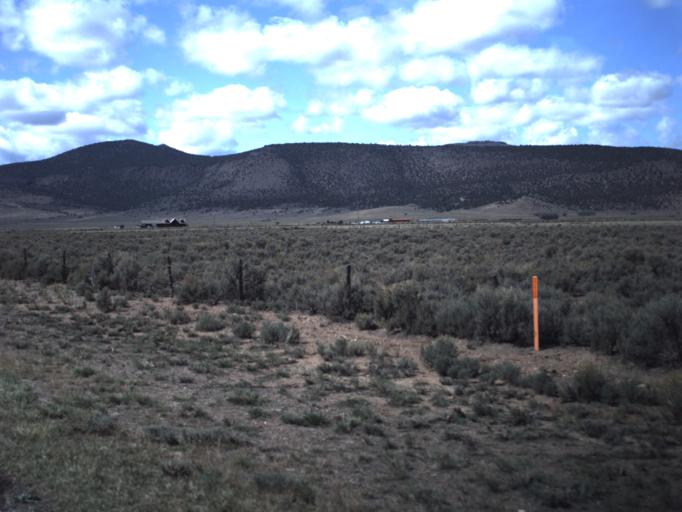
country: US
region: Utah
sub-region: Wayne County
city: Loa
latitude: 38.4792
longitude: -111.8970
